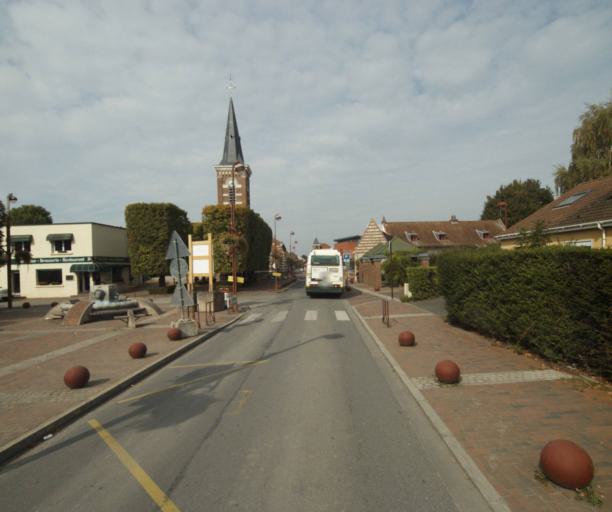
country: FR
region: Nord-Pas-de-Calais
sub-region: Departement du Nord
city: Templemars
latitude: 50.5711
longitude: 3.0544
